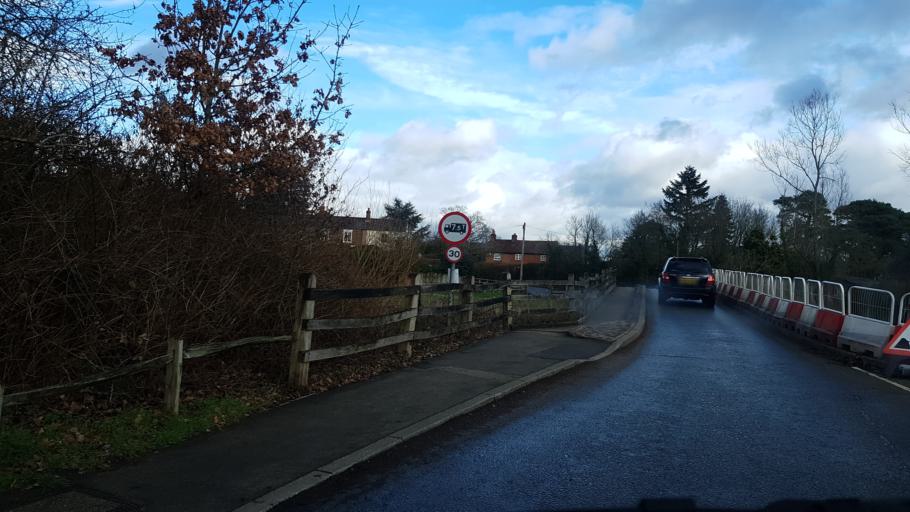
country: GB
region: England
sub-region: Surrey
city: Elstead
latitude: 51.1836
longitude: -0.7516
